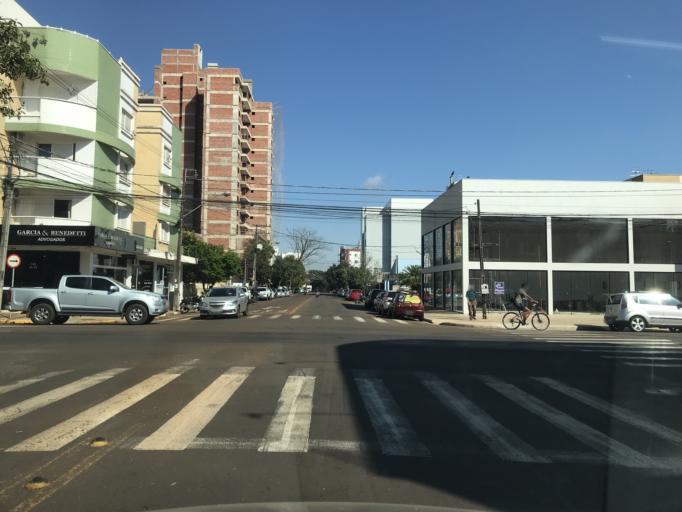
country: BR
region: Parana
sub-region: Toledo
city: Toledo
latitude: -24.7238
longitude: -53.7393
